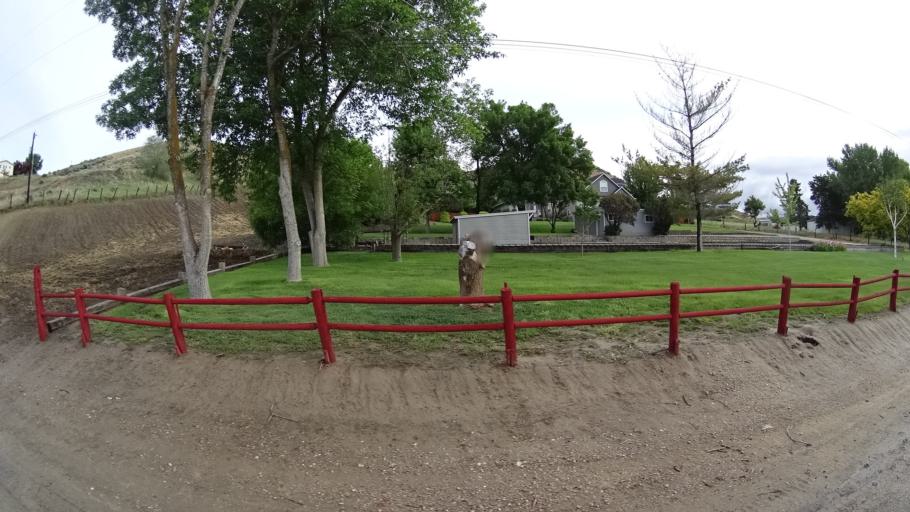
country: US
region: Idaho
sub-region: Ada County
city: Eagle
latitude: 43.7354
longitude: -116.3085
